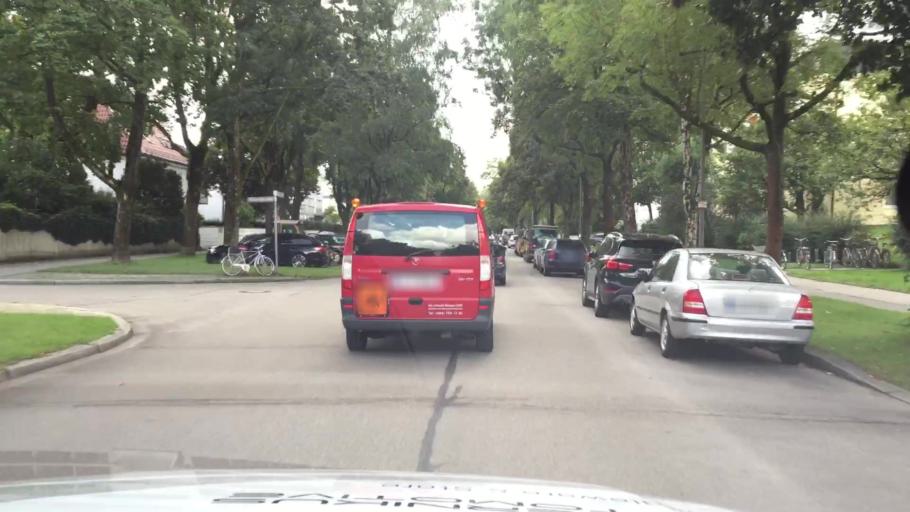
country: DE
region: Bavaria
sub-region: Upper Bavaria
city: Bogenhausen
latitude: 48.1684
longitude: 11.6017
